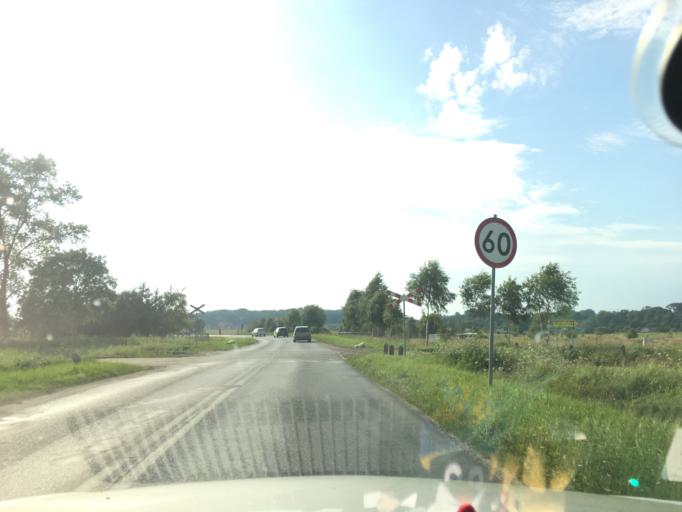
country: PL
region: West Pomeranian Voivodeship
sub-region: Powiat gryficki
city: Rewal
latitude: 54.0826
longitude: 15.0478
